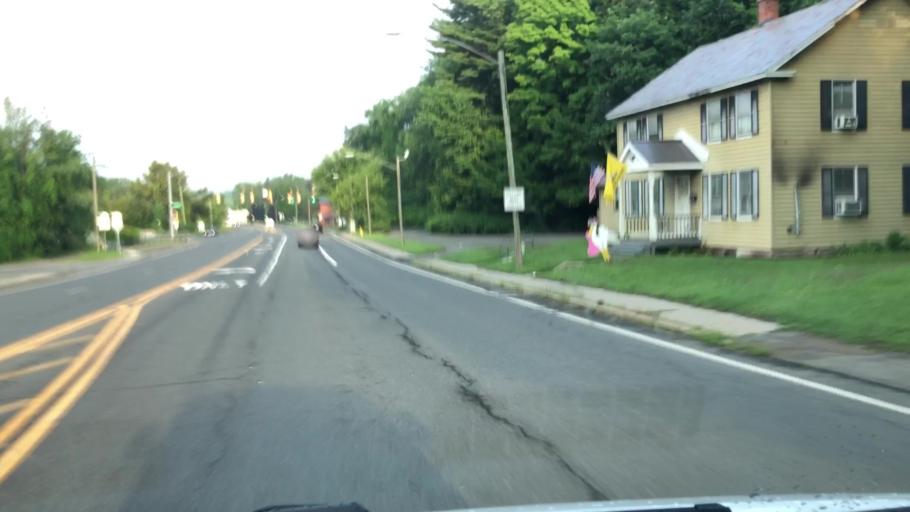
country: US
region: Massachusetts
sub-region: Berkshire County
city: Dalton
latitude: 42.4701
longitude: -73.1953
